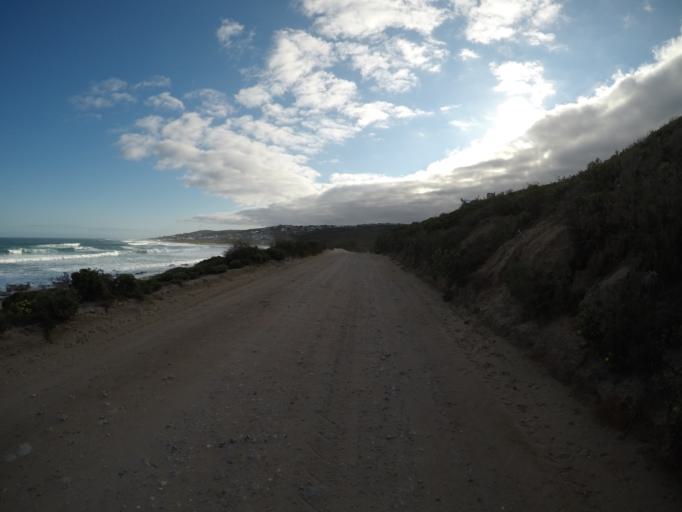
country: ZA
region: Western Cape
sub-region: Eden District Municipality
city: Riversdale
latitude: -34.4190
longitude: 21.3566
